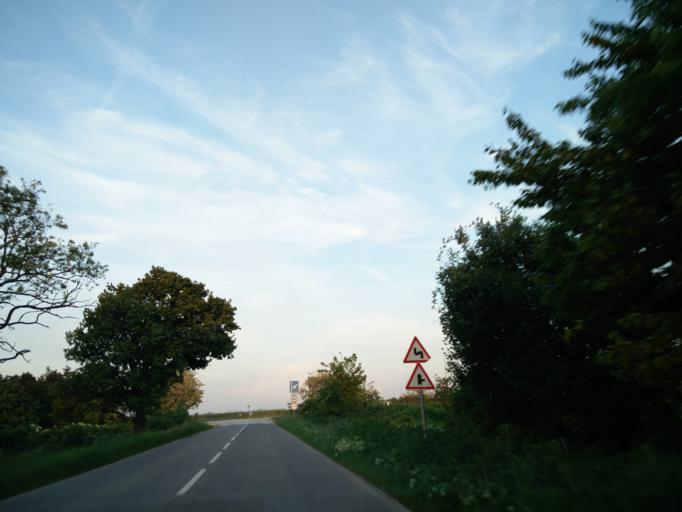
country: HU
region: Fejer
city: Etyek
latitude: 47.4441
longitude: 18.7275
